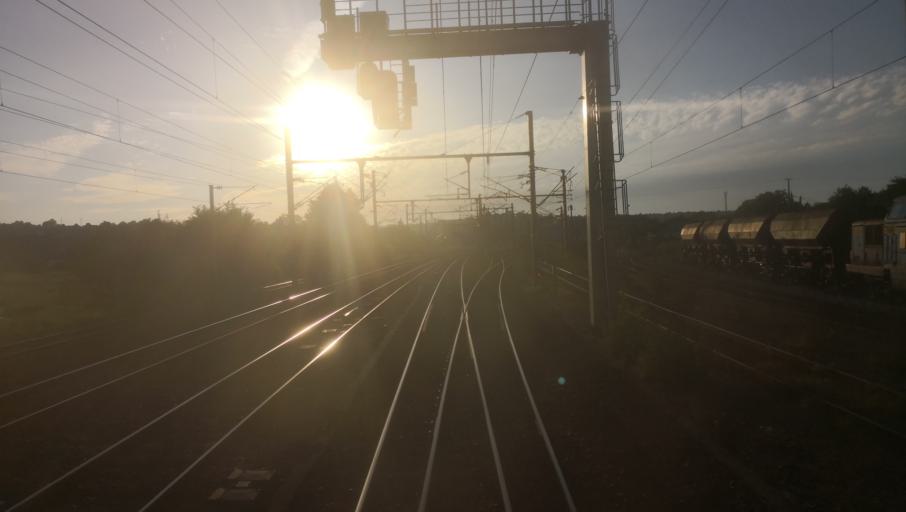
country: FR
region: Lower Normandy
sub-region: Departement du Calvados
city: Lisieux
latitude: 49.1355
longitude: 0.2344
